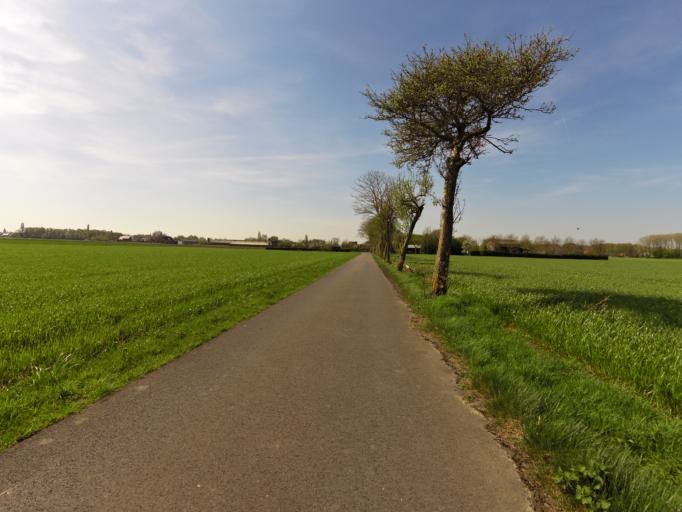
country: BE
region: Flanders
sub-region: Provincie West-Vlaanderen
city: Ichtegem
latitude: 51.1066
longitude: 3.0177
